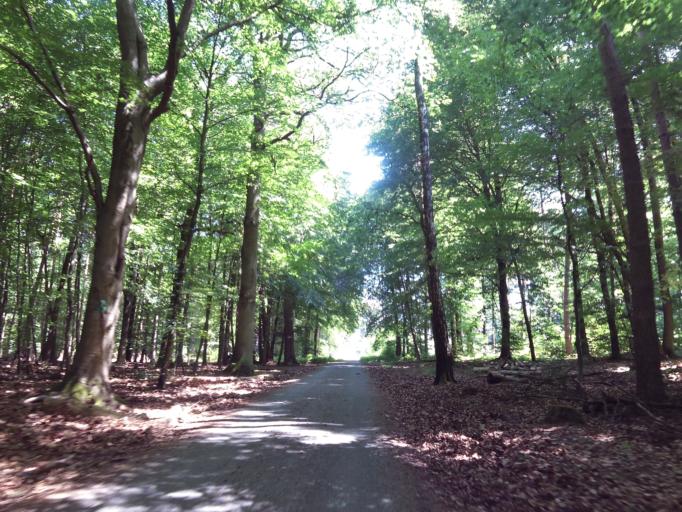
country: DE
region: Hesse
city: Langen
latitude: 50.0067
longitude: 8.6407
